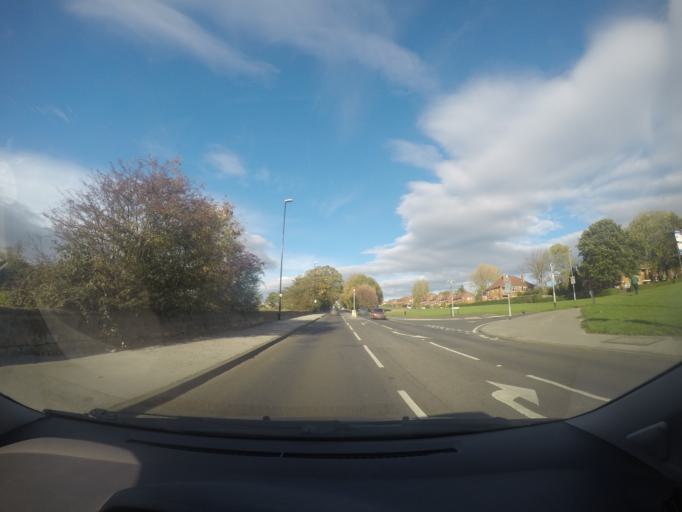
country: GB
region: England
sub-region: City and Borough of Leeds
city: Shadwell
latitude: 53.8320
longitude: -1.4753
